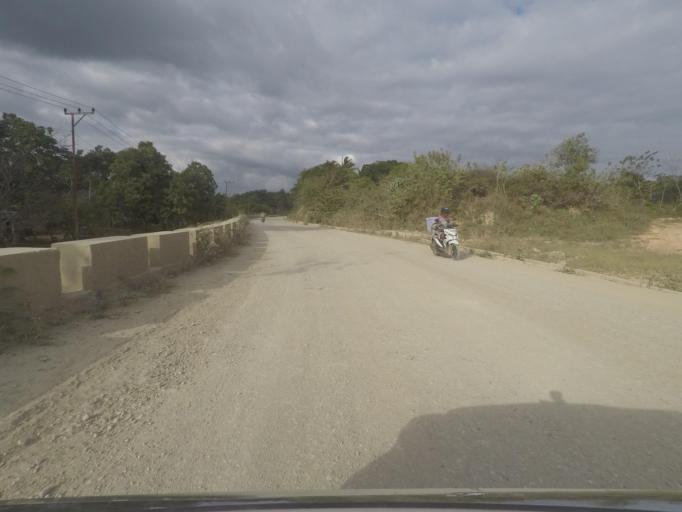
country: TL
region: Baucau
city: Venilale
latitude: -8.5857
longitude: 126.3881
